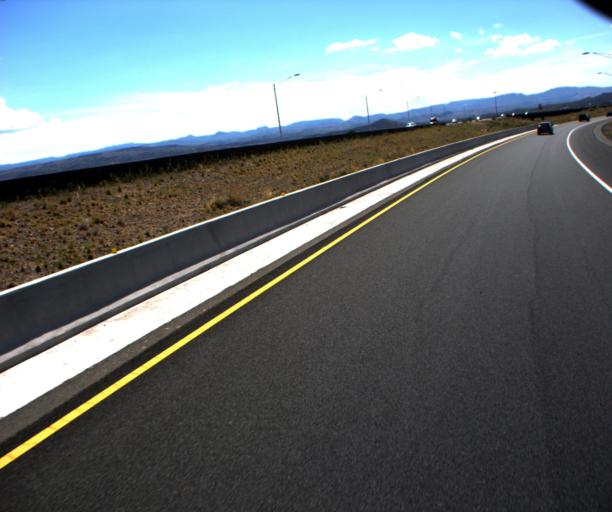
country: US
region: Arizona
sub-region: Yavapai County
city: Cordes Lakes
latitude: 34.3318
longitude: -112.1249
